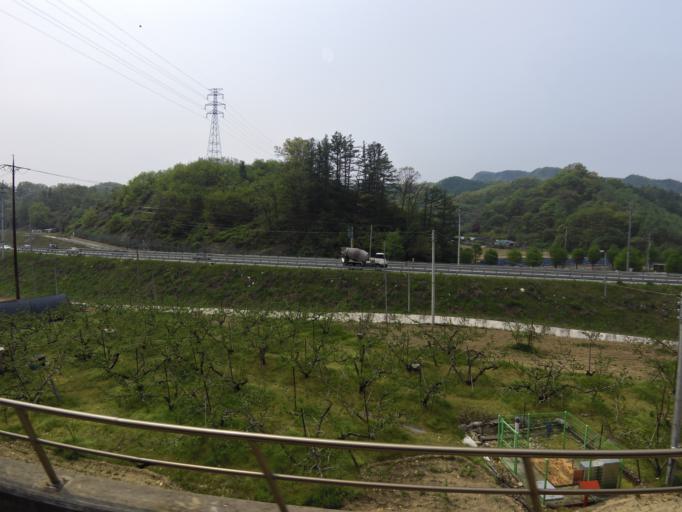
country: KR
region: Chungcheongbuk-do
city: Okcheon
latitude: 36.3255
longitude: 127.5432
